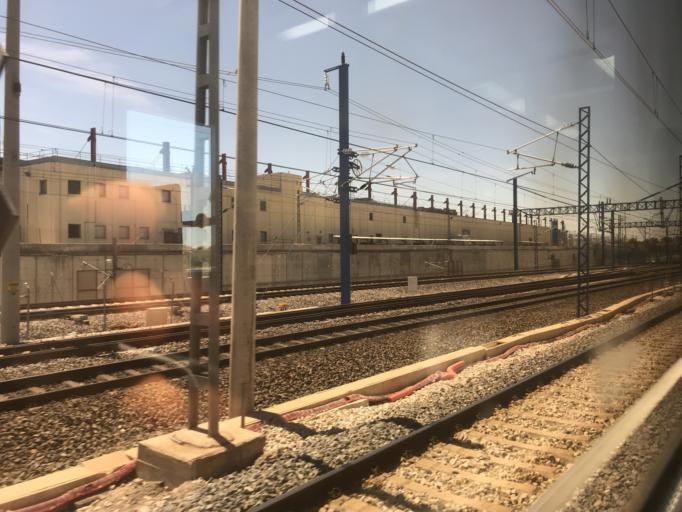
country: ES
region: Madrid
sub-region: Provincia de Madrid
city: Puente de Vallecas
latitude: 40.3861
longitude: -3.6770
